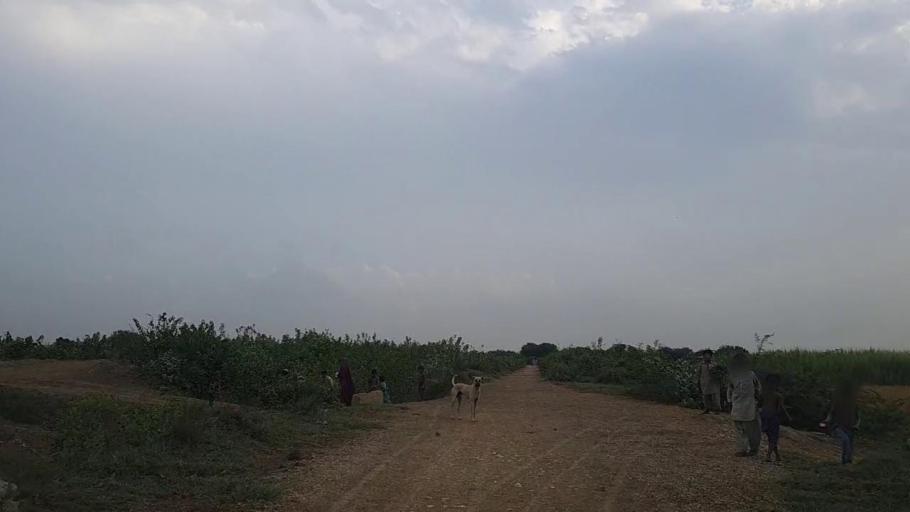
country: PK
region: Sindh
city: Daro Mehar
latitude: 24.7590
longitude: 68.1572
